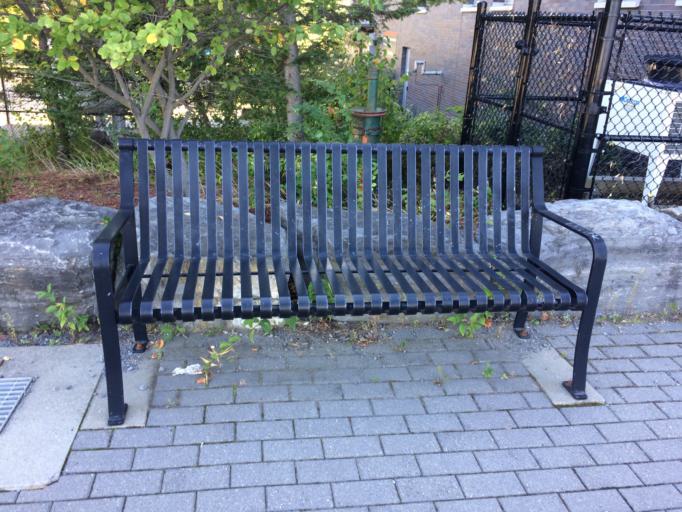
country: CA
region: Ontario
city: Ottawa
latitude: 45.3844
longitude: -75.6925
